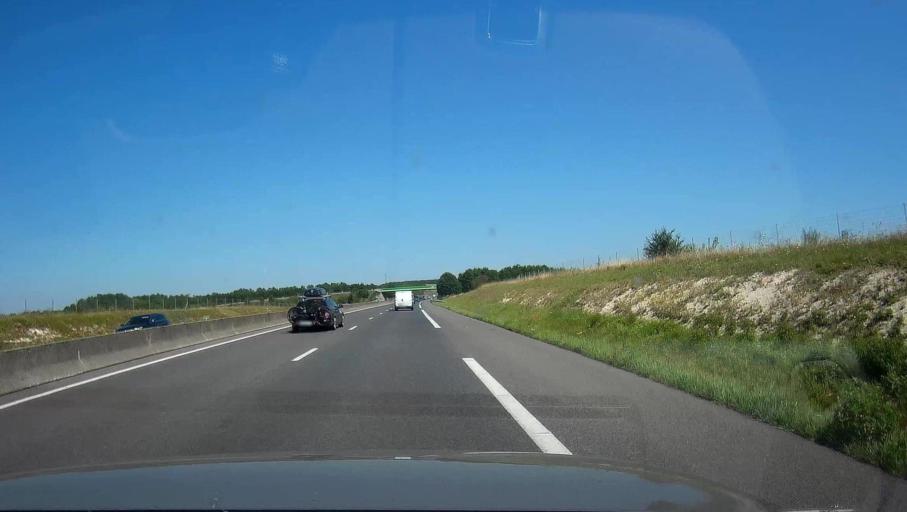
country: FR
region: Champagne-Ardenne
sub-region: Departement de l'Aube
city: Mailly-le-Camp
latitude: 48.7895
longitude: 4.2682
